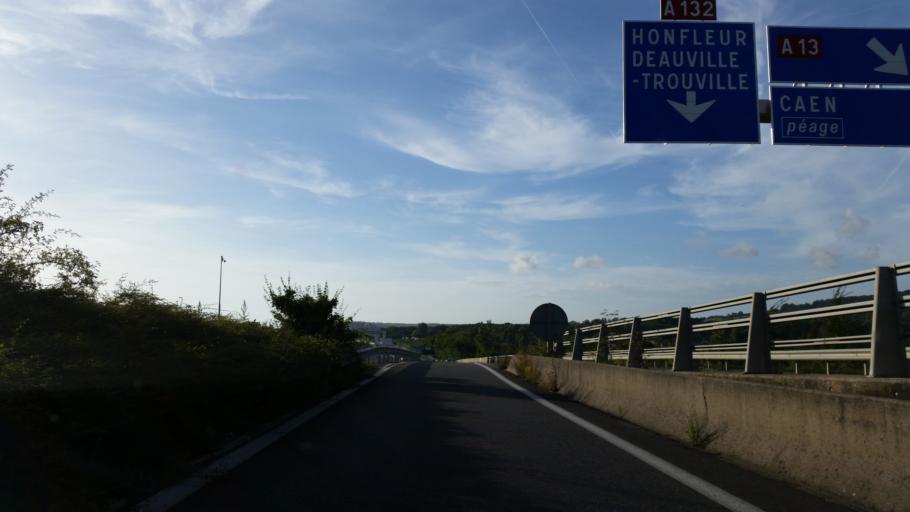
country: FR
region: Lower Normandy
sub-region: Departement du Calvados
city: Saint-Gatien-des-Bois
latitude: 49.2903
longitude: 0.2030
